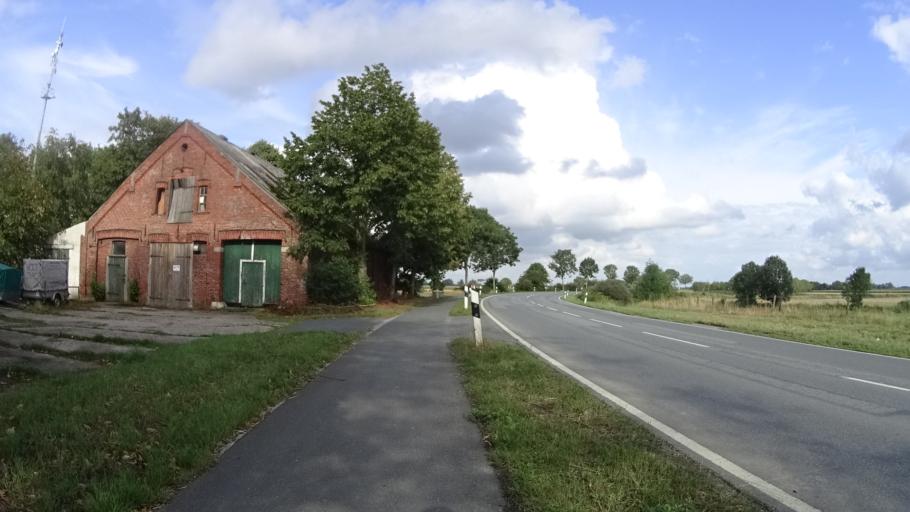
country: DE
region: Lower Saxony
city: Varel
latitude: 53.3938
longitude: 8.1750
